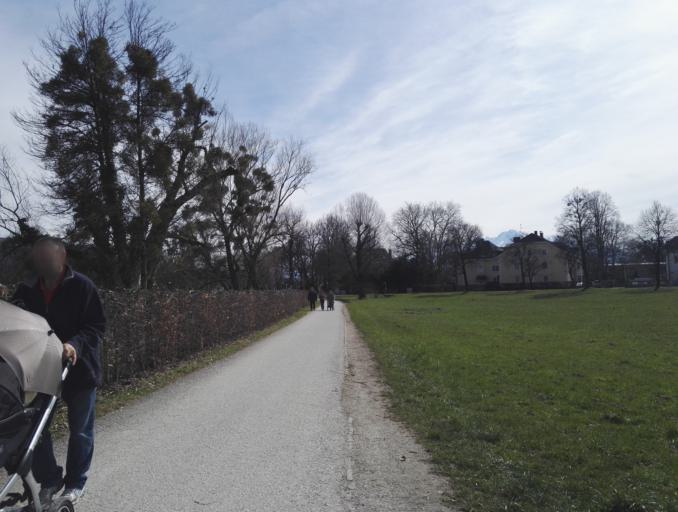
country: AT
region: Salzburg
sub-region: Salzburg Stadt
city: Salzburg
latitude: 47.7869
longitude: 13.0570
